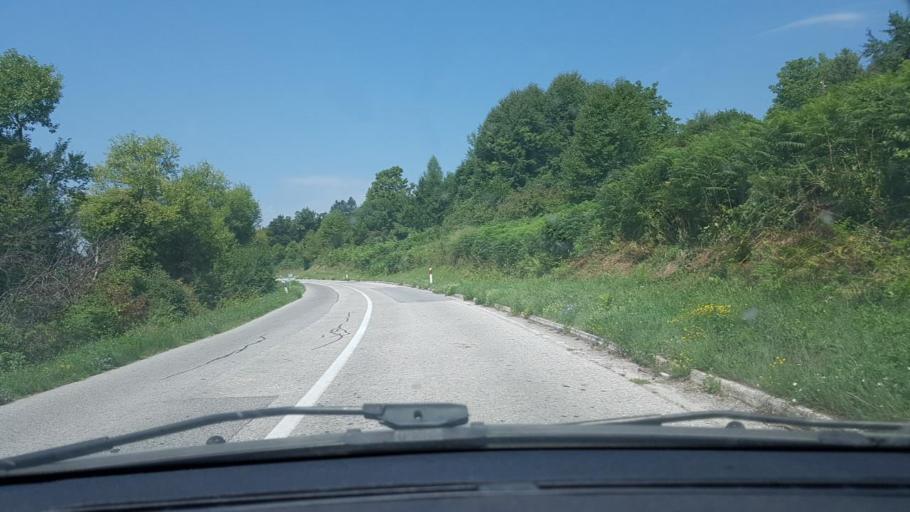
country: HR
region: Karlovacka
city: Vojnic
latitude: 45.2483
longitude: 15.7155
